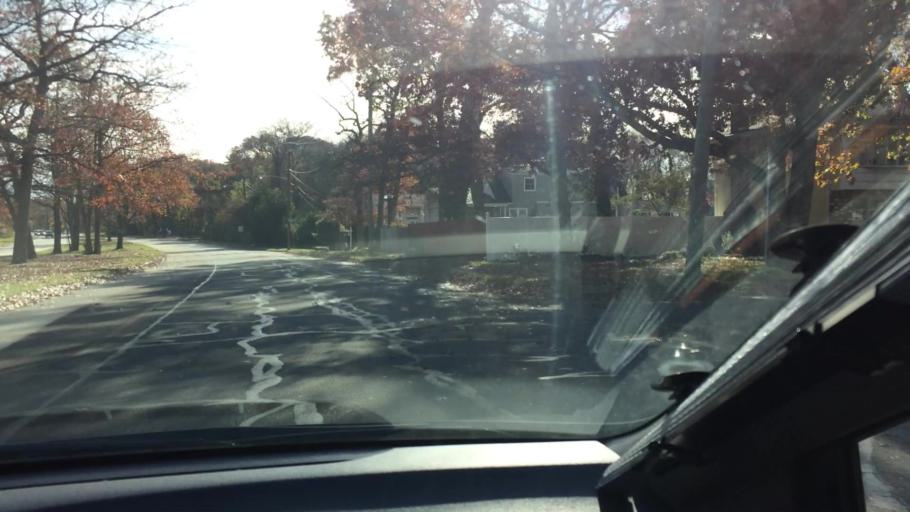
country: US
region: New York
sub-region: Suffolk County
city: West Babylon
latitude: 40.7362
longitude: -73.3466
